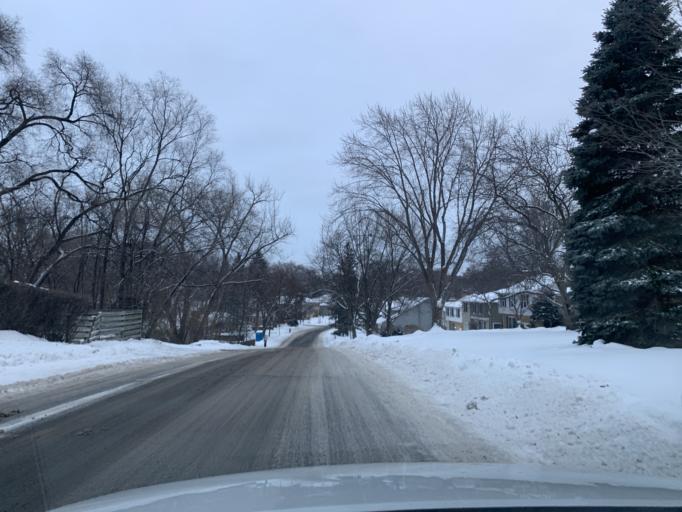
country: US
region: Minnesota
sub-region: Hennepin County
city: Saint Louis Park
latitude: 44.9283
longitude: -93.3423
